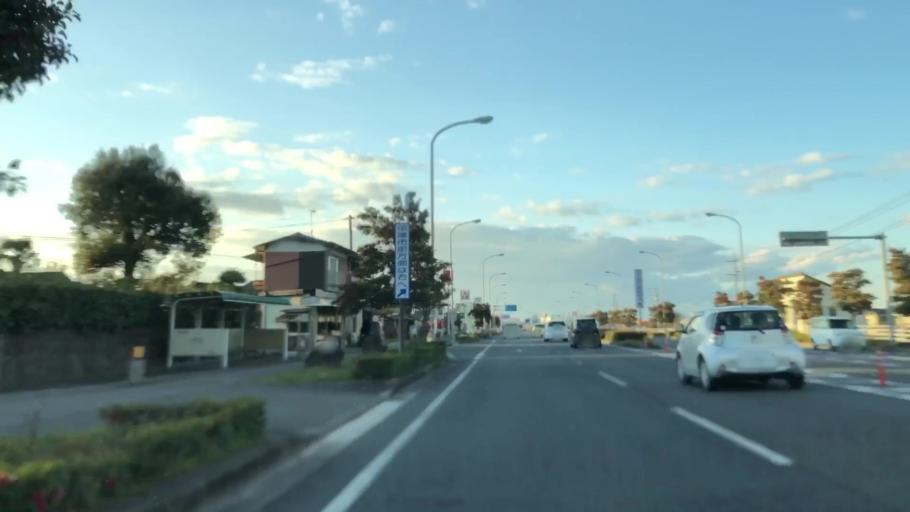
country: JP
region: Fukuoka
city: Nakatsu
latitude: 33.5468
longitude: 131.2814
